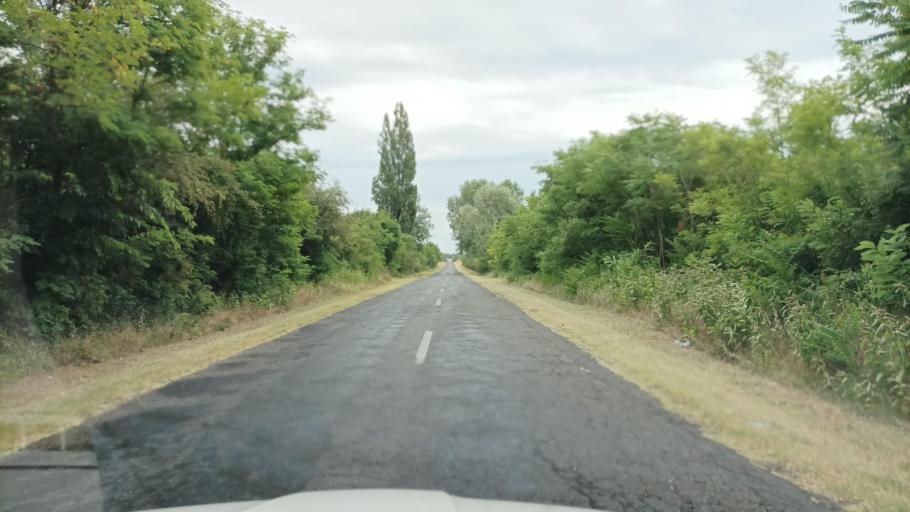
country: HU
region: Pest
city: Dabas
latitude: 47.1320
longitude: 19.3378
